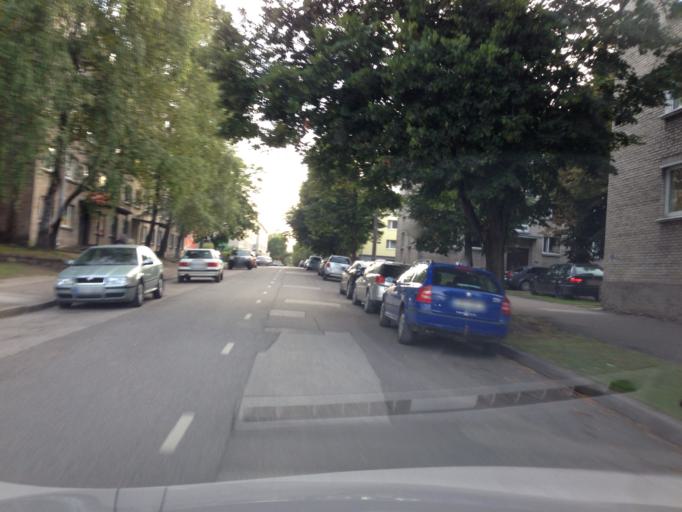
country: EE
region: Tartu
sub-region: Tartu linn
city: Tartu
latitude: 58.3768
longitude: 26.7192
